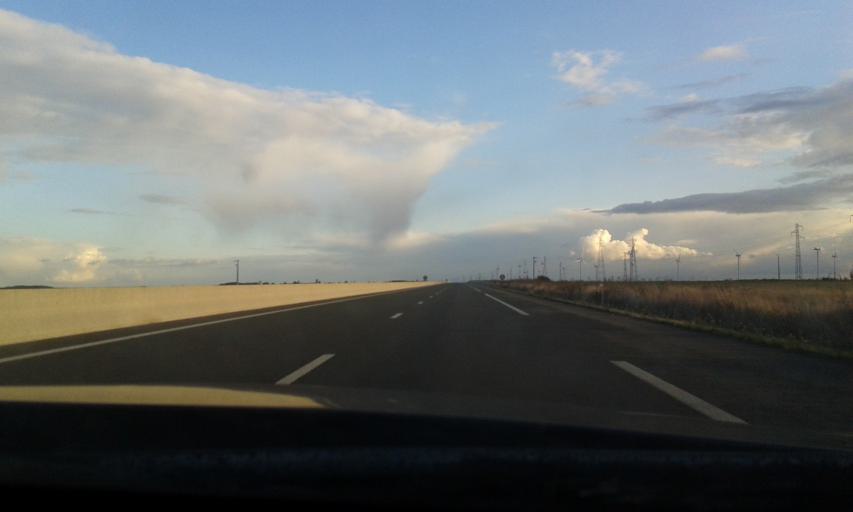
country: FR
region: Centre
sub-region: Departement d'Eure-et-Loir
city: Sours
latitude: 48.3459
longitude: 1.6284
